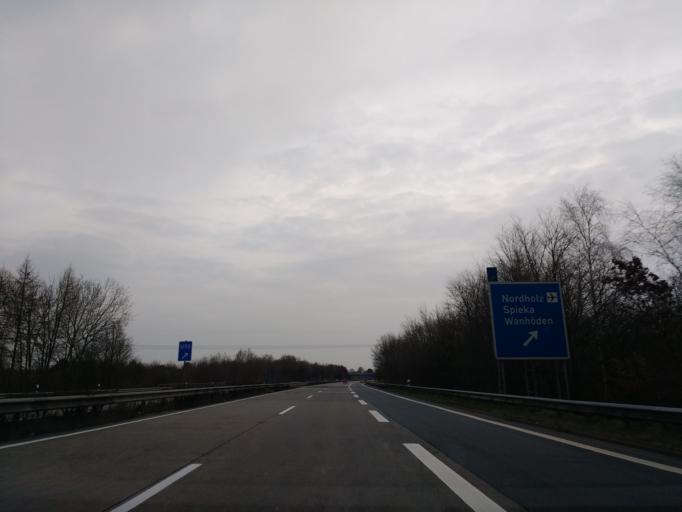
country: DE
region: Lower Saxony
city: Midlum
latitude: 53.7456
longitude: 8.6684
